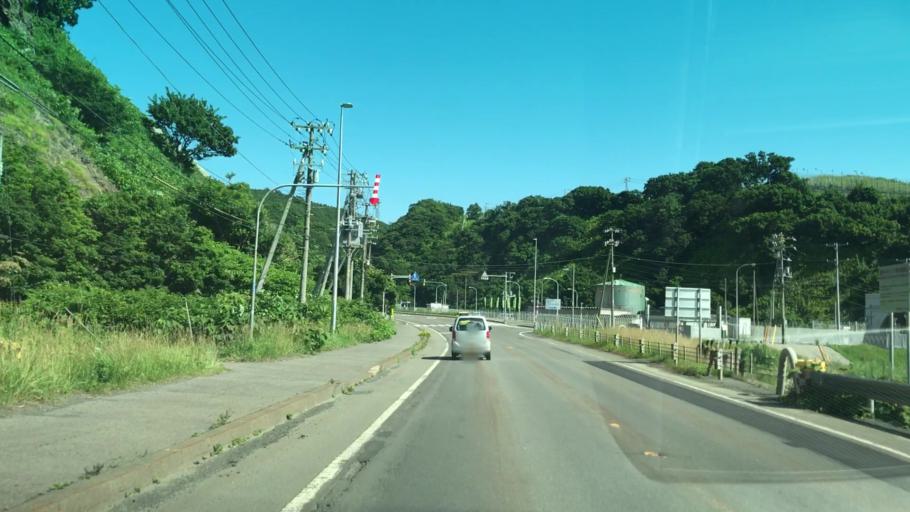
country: JP
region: Hokkaido
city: Iwanai
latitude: 43.0430
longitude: 140.5084
